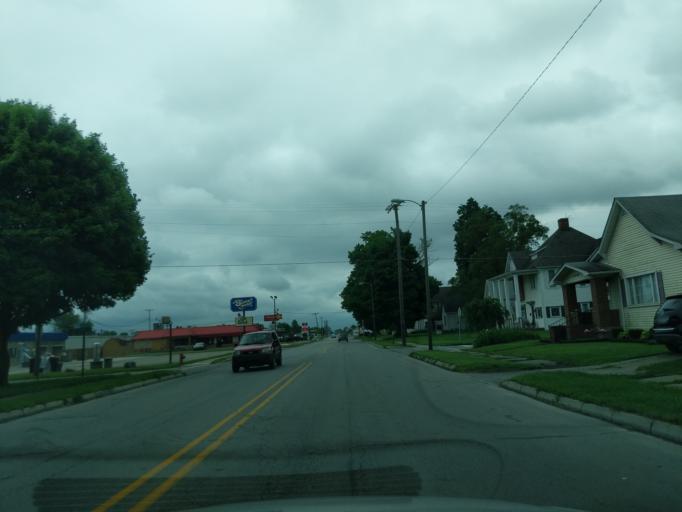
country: US
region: Indiana
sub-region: Madison County
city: Elwood
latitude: 40.2770
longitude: -85.8252
